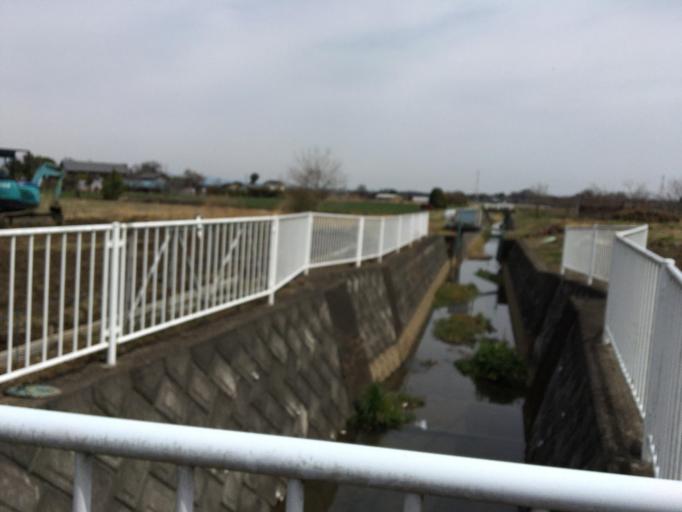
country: JP
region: Saitama
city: Yorii
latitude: 36.1457
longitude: 139.2074
